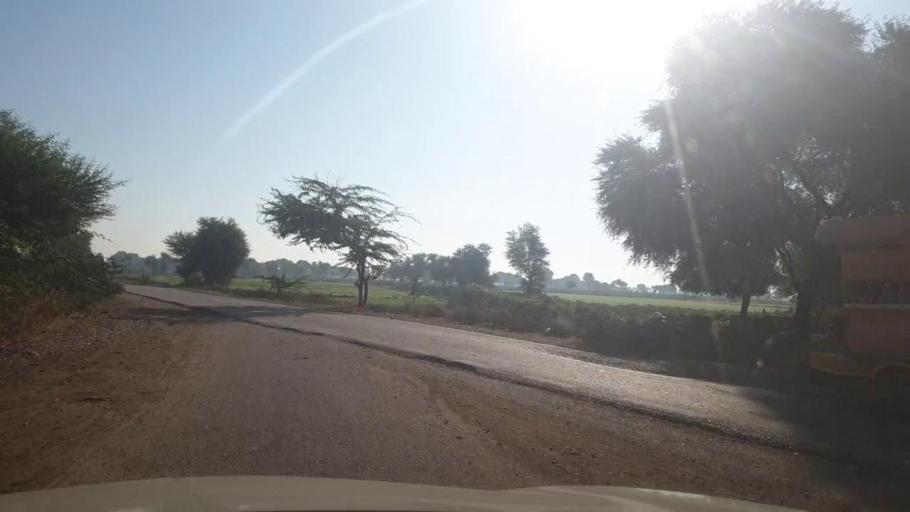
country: PK
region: Sindh
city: Bhan
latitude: 26.5412
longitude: 67.6861
